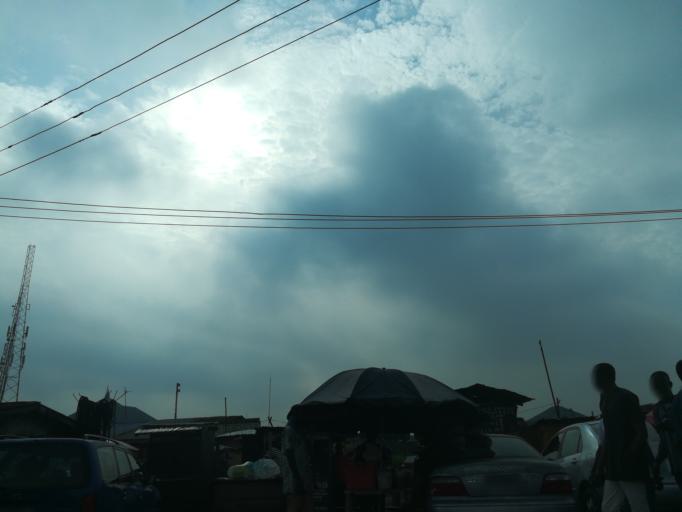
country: NG
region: Rivers
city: Port Harcourt
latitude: 4.8005
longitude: 6.9949
